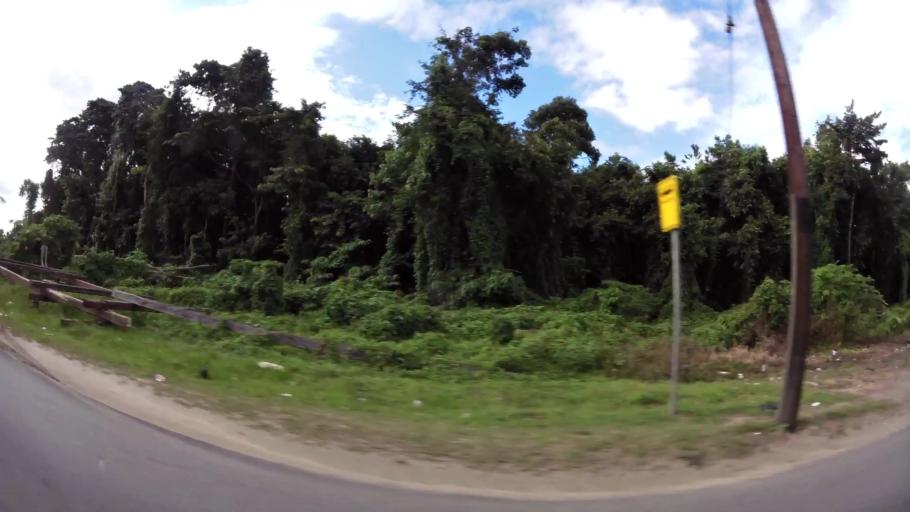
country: SR
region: Paramaribo
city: Paramaribo
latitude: 5.8452
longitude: -55.2239
